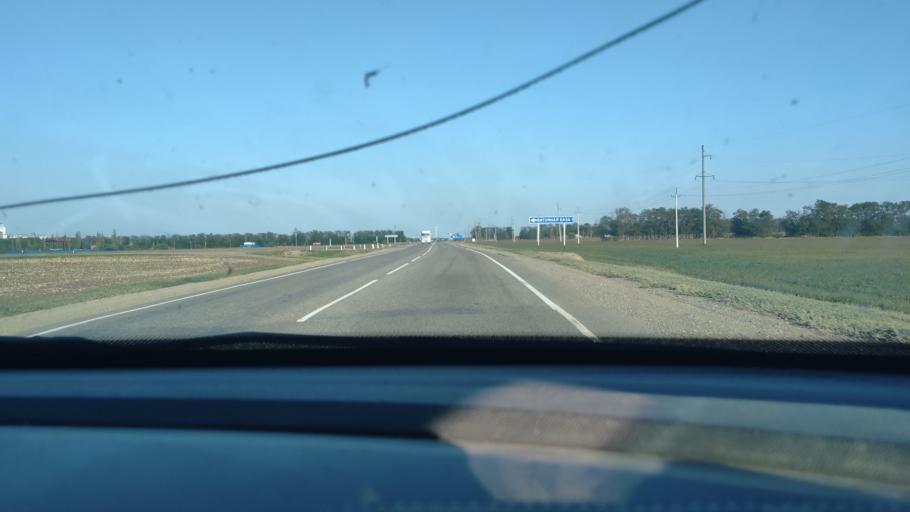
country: RU
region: Krasnodarskiy
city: Staroshcherbinovskaya
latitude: 46.6105
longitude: 38.6453
